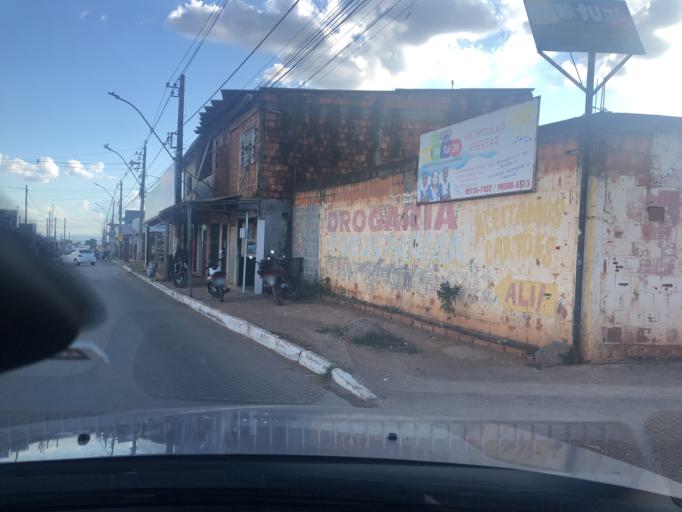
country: BR
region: Federal District
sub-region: Brasilia
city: Brasilia
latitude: -15.8341
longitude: -48.1338
